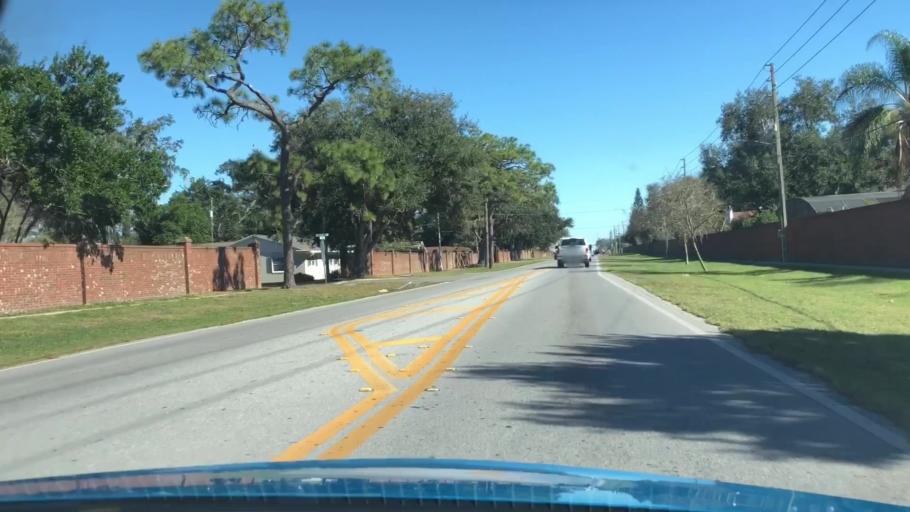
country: US
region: Florida
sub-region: Orange County
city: Conway
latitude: 28.4805
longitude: -81.3367
